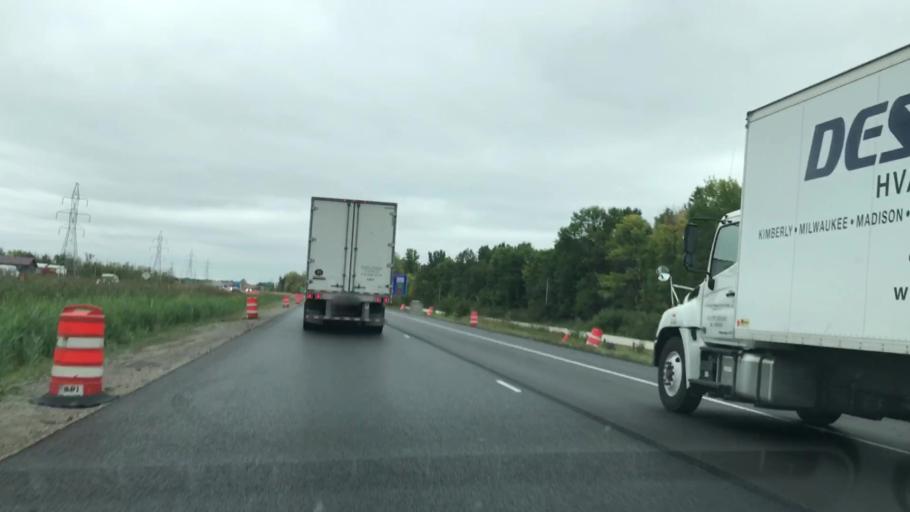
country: US
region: Wisconsin
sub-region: Brown County
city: Suamico
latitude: 44.6049
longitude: -88.0504
